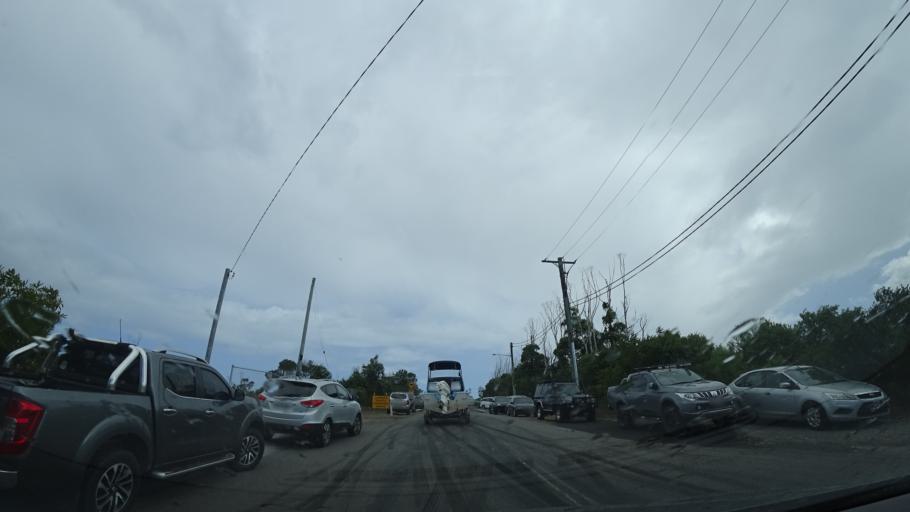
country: AU
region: New South Wales
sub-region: Wyong Shire
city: Kingfisher Shores
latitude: -33.1602
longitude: 151.6272
